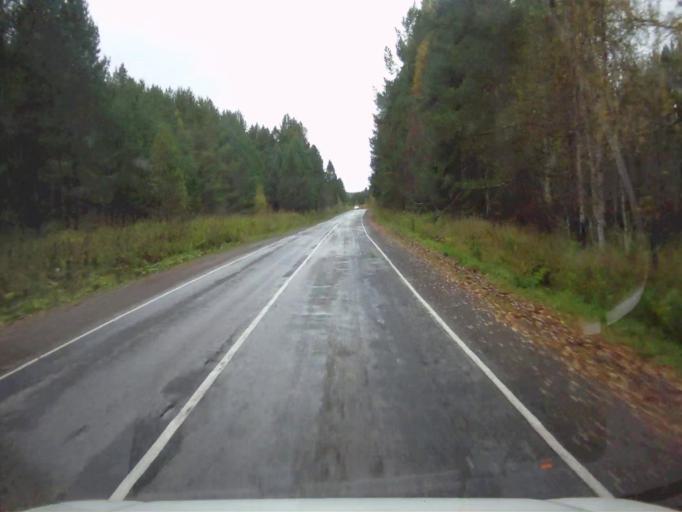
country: RU
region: Chelyabinsk
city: Nyazepetrovsk
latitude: 56.0632
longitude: 59.7057
